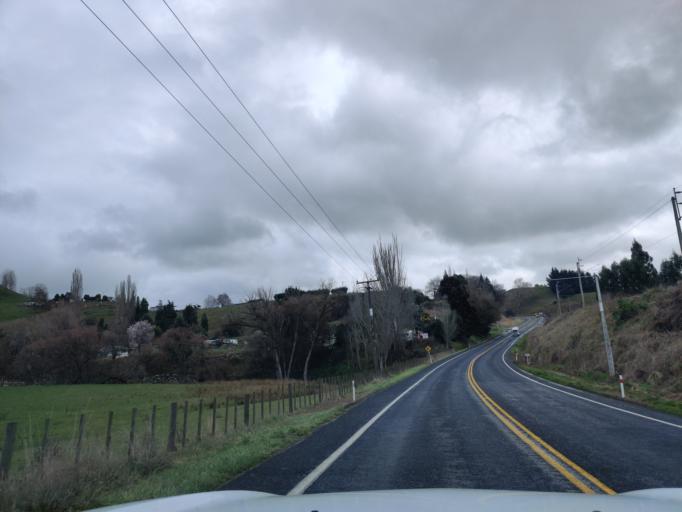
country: NZ
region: Manawatu-Wanganui
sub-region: Ruapehu District
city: Waiouru
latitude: -39.6893
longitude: 175.8084
